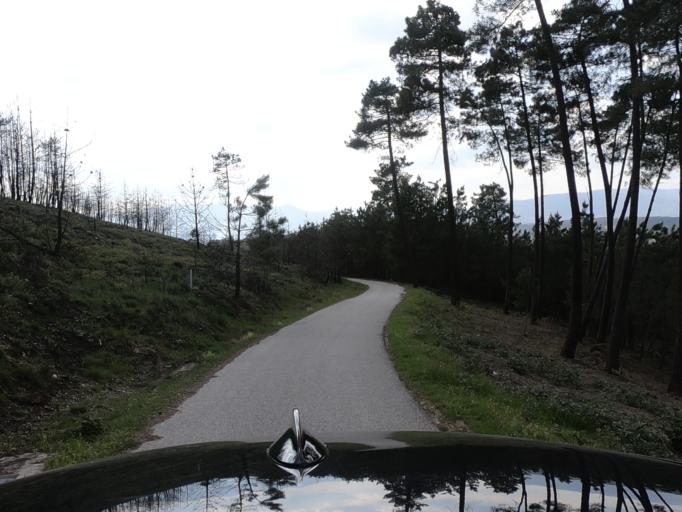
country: PT
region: Vila Real
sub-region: Sabrosa
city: Vilela
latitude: 41.2379
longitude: -7.6704
